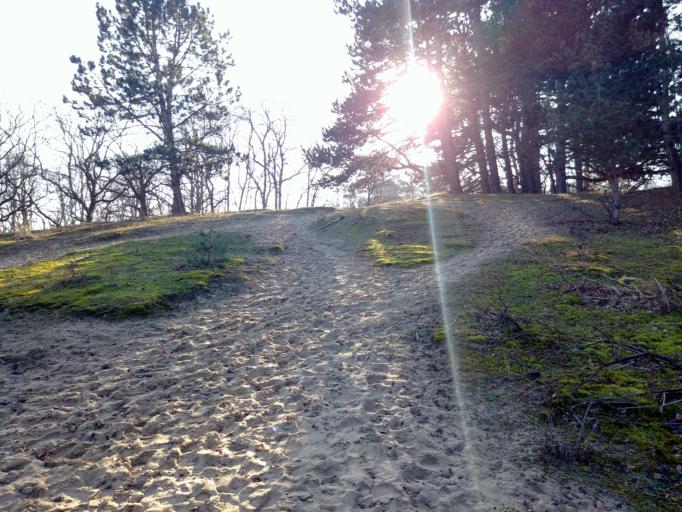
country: NL
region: North Holland
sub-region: Gemeente Bloemendaal
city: Bennebroek
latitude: 52.3502
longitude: 4.5735
